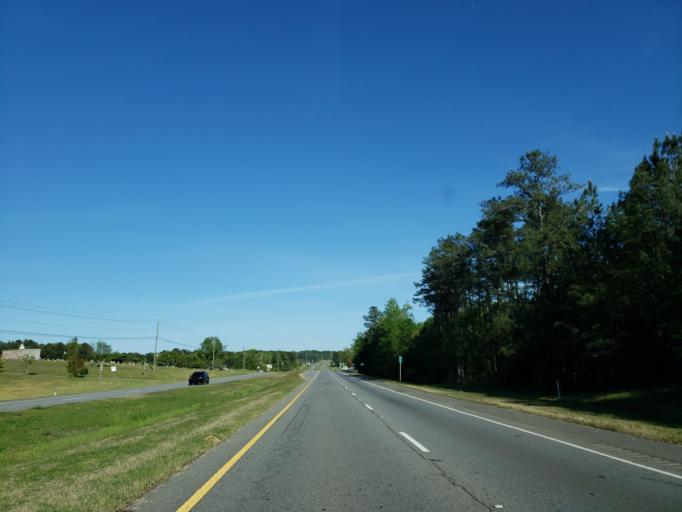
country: US
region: Georgia
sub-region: Polk County
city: Cedartown
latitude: 34.0169
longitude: -85.2032
